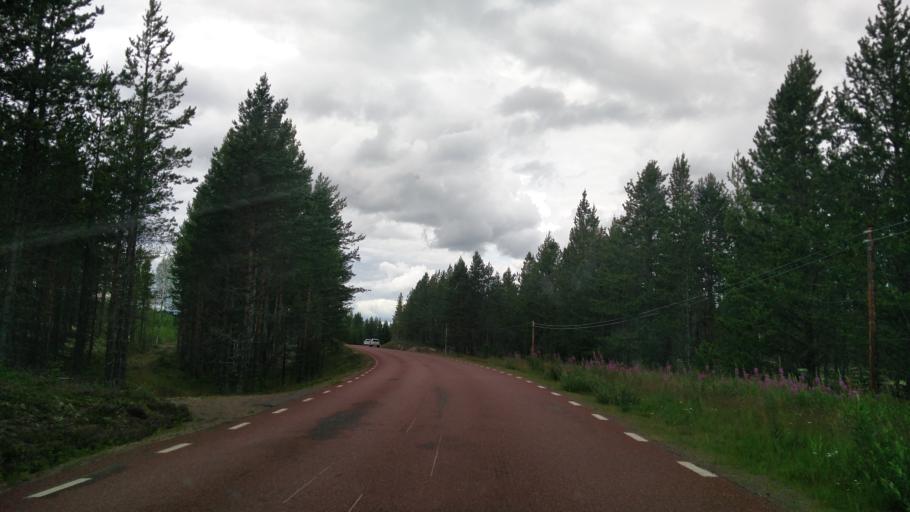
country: NO
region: Hedmark
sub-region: Trysil
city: Innbygda
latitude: 61.1450
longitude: 12.8062
